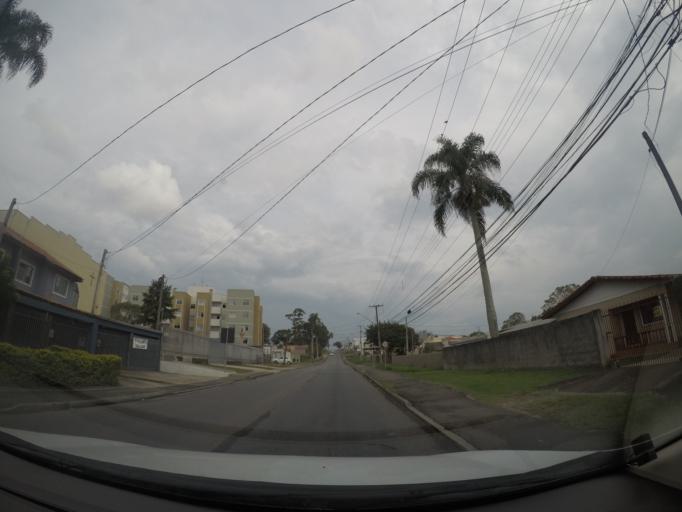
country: BR
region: Parana
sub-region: Sao Jose Dos Pinhais
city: Sao Jose dos Pinhais
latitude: -25.5223
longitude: -49.2612
